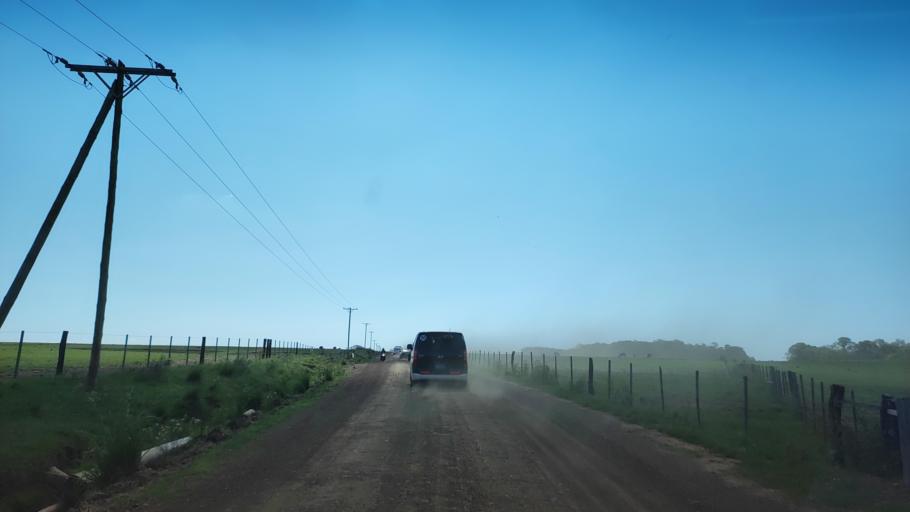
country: PY
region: Itapua
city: Carmen del Parana
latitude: -27.4121
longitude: -56.1415
